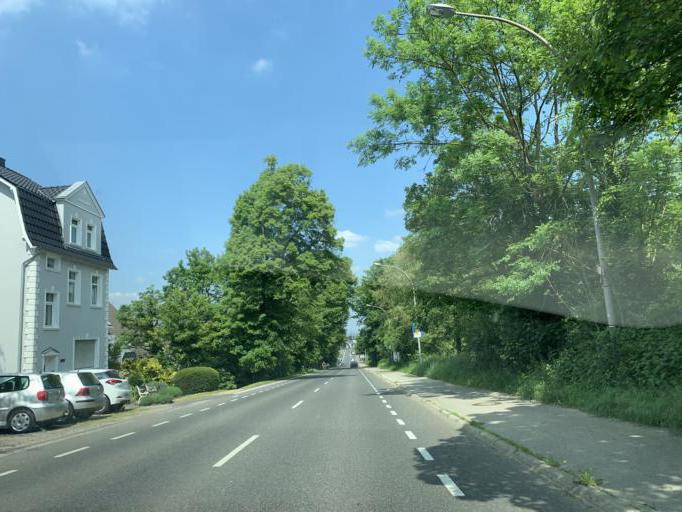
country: DE
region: North Rhine-Westphalia
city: Bruhl
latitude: 50.8080
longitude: 6.8808
